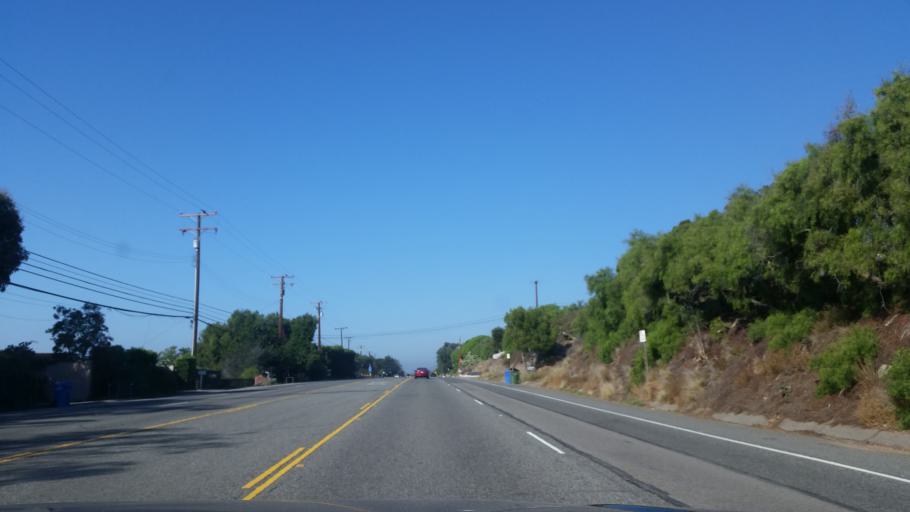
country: US
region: California
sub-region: Los Angeles County
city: Malibu
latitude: 34.0425
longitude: -118.9019
